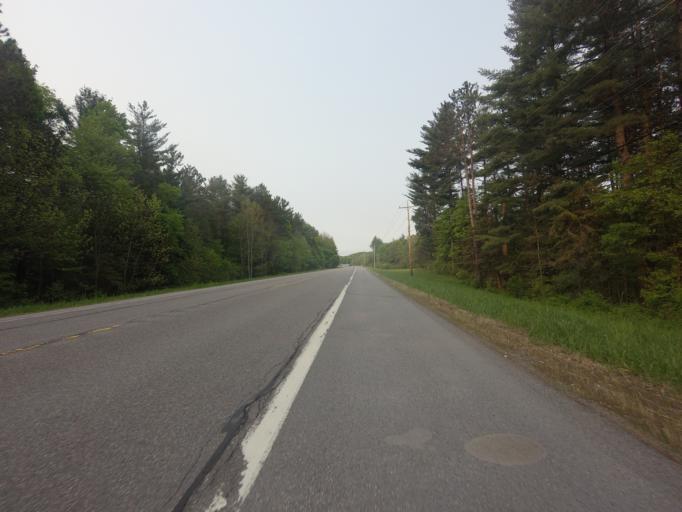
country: US
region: New York
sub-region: Jefferson County
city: Carthage
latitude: 44.1049
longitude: -75.4092
